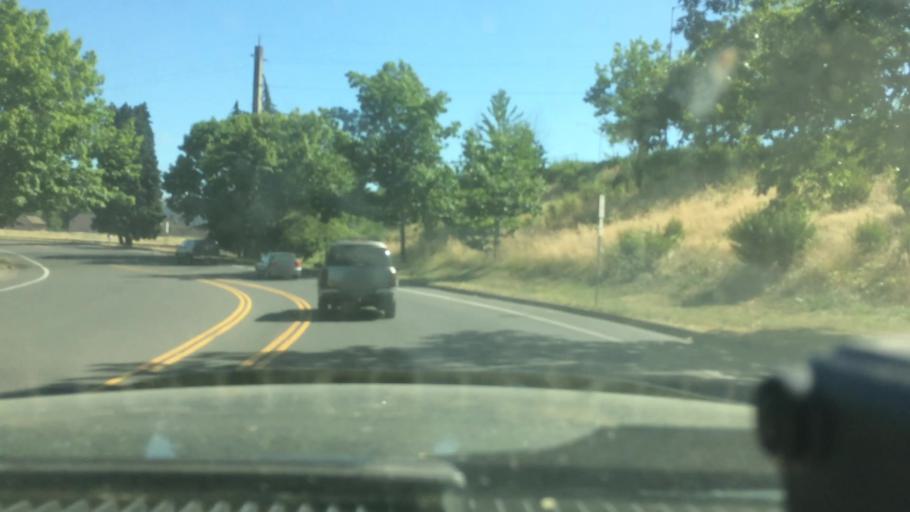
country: US
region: Oregon
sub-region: Lane County
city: Eugene
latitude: 44.0634
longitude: -123.1167
